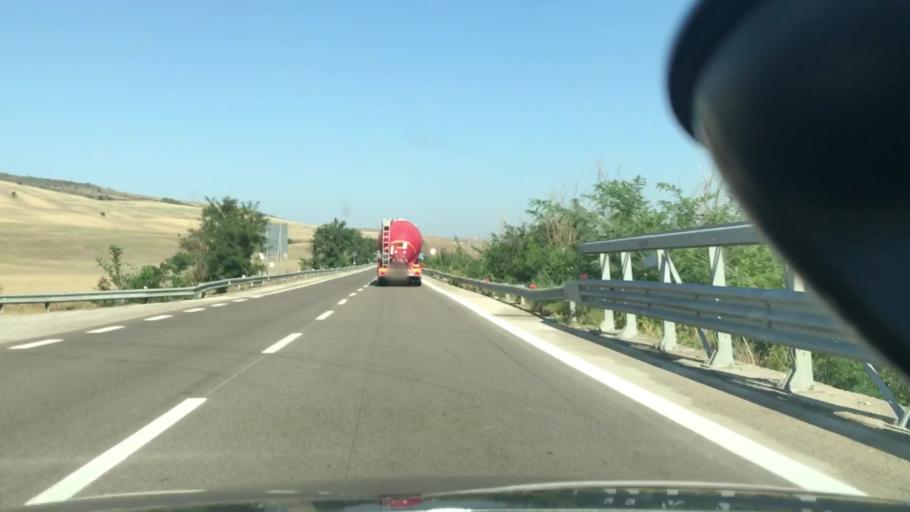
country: IT
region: Basilicate
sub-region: Provincia di Matera
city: Irsina
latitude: 40.7923
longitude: 16.2812
